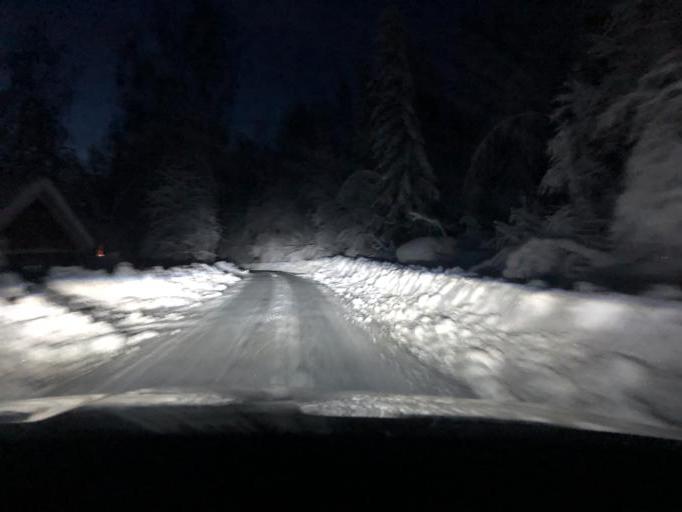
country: SE
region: Vaesternorrland
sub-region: Kramfors Kommun
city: Bollstabruk
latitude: 63.0539
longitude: 17.6824
